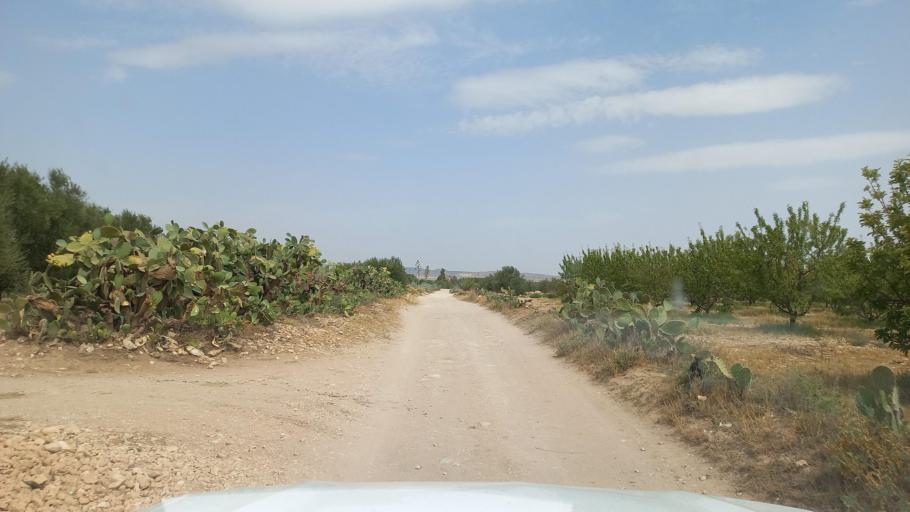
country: TN
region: Al Qasrayn
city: Kasserine
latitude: 35.2770
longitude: 9.0262
